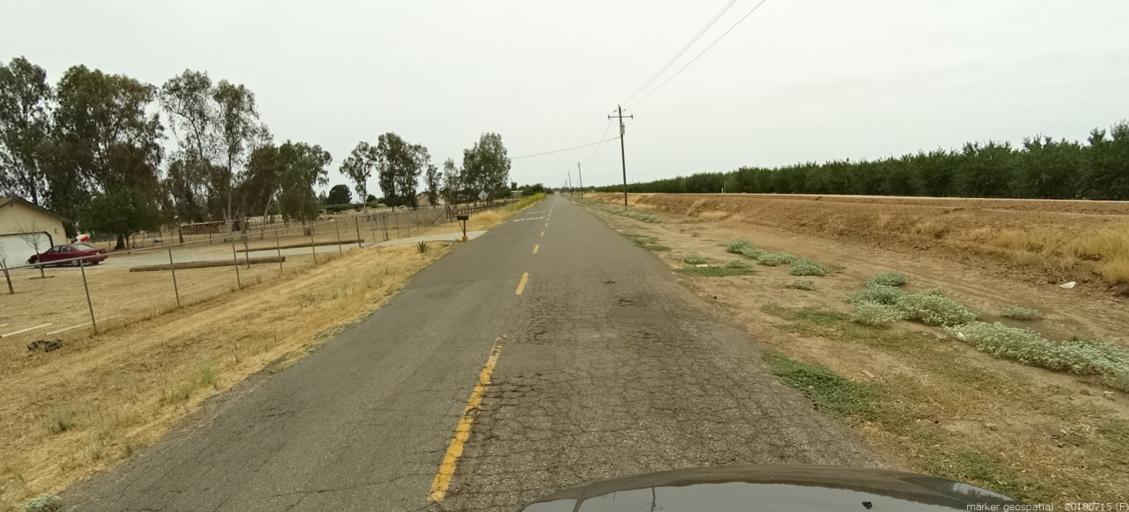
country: US
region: California
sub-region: Madera County
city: Madera Acres
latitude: 37.0255
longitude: -120.1090
